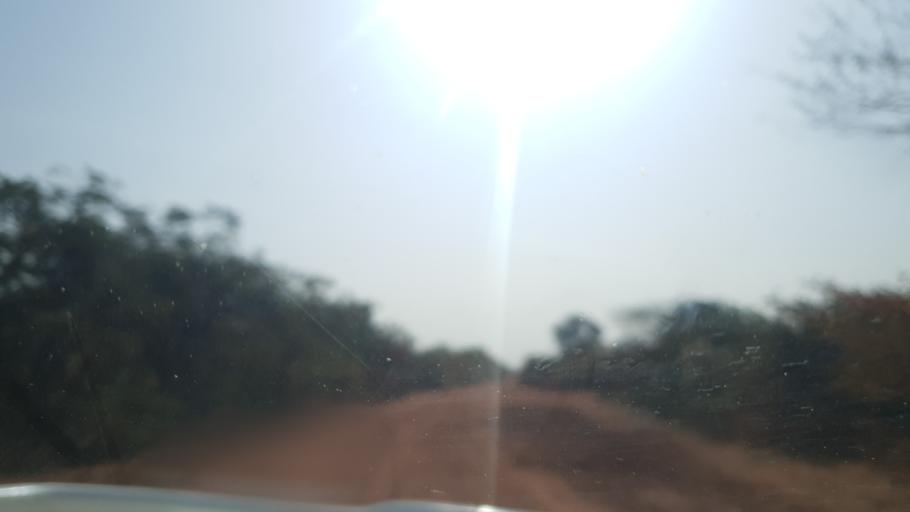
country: ML
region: Koulikoro
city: Dioila
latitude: 12.6976
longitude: -6.7585
